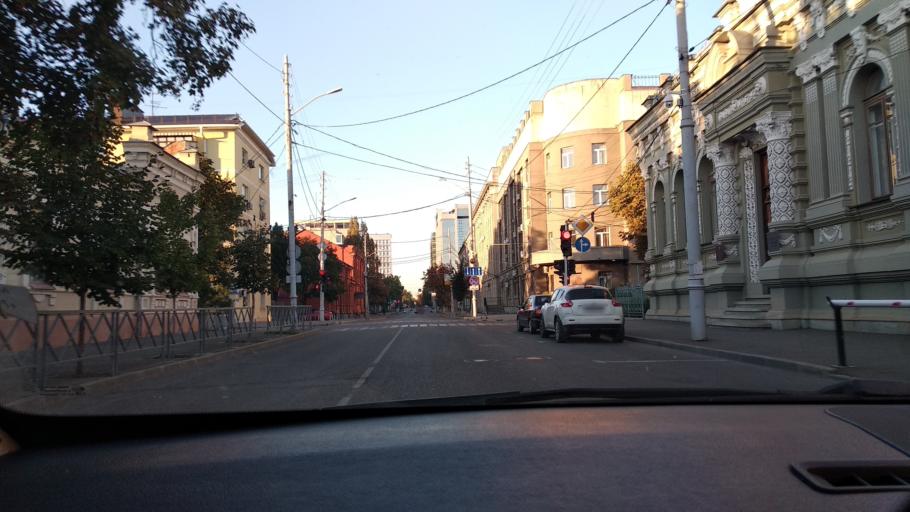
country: RU
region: Krasnodarskiy
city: Krasnodar
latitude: 45.0186
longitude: 38.9707
